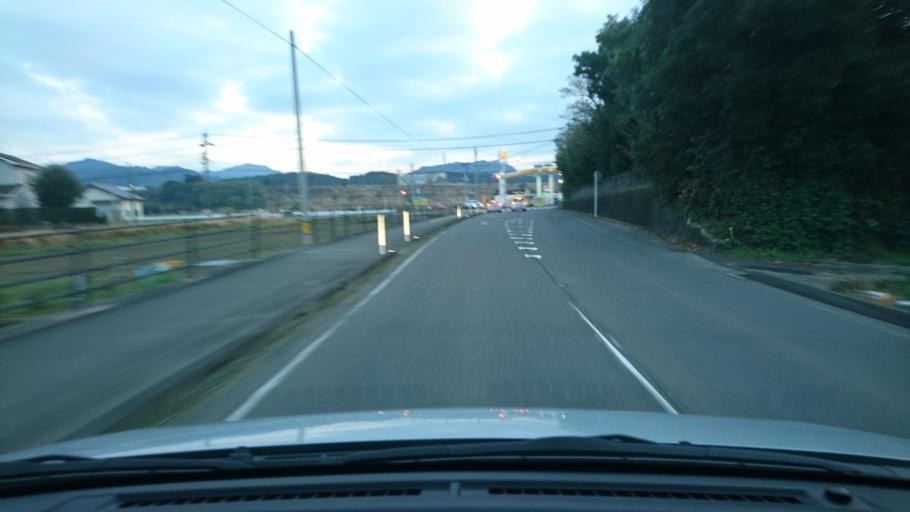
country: JP
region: Miyazaki
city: Miyazaki-shi
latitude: 31.8438
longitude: 131.4076
